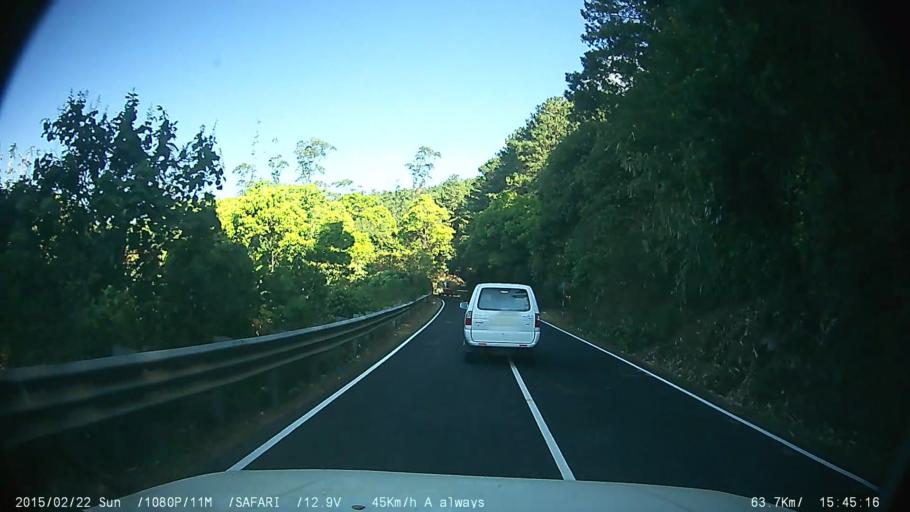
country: IN
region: Kerala
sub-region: Kottayam
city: Erattupetta
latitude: 9.5808
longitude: 76.9773
